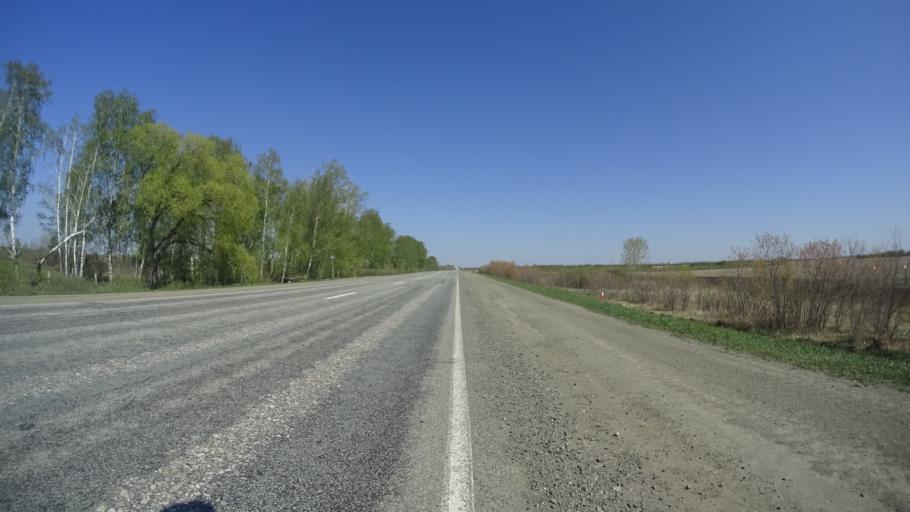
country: RU
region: Chelyabinsk
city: Troitsk
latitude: 54.1971
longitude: 61.4326
